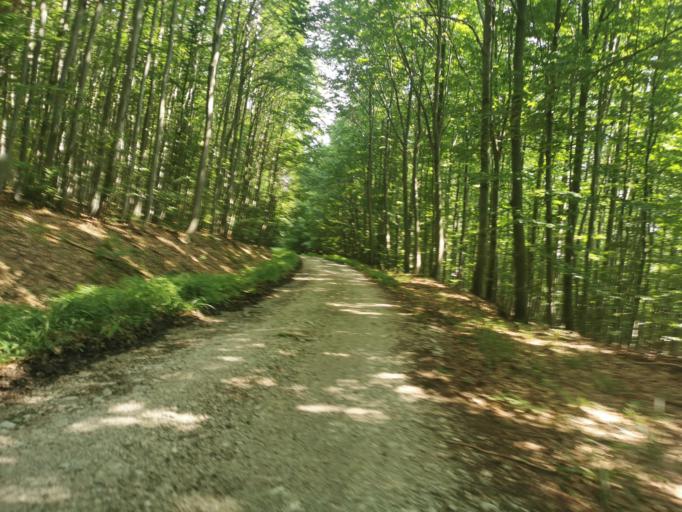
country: SK
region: Trenciansky
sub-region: Okres Myjava
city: Myjava
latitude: 48.8204
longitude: 17.5614
